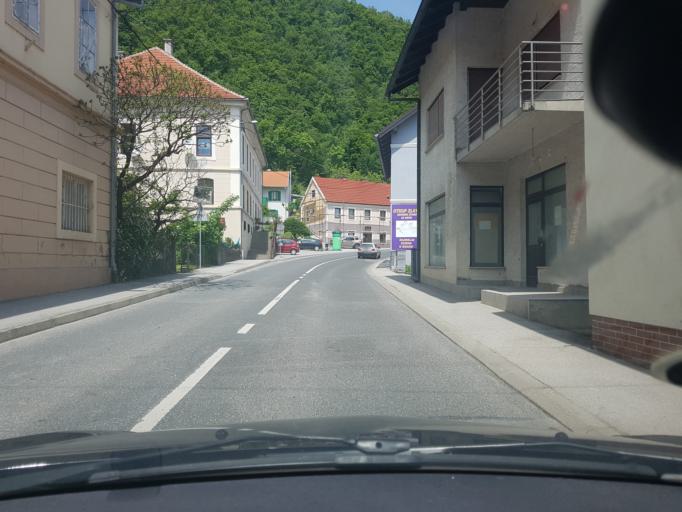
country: HR
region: Krapinsko-Zagorska
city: Pregrada
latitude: 46.1654
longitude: 15.7505
